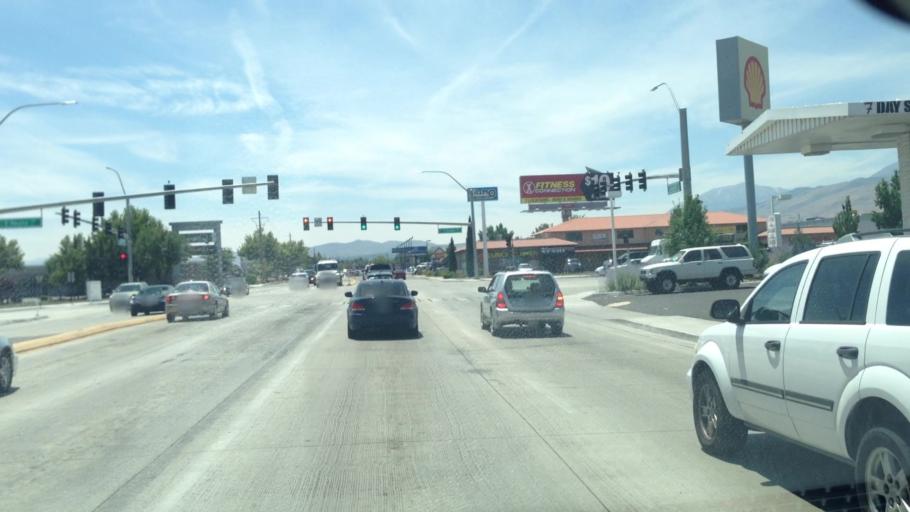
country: US
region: Nevada
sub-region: Washoe County
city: Reno
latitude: 39.4935
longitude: -119.7892
